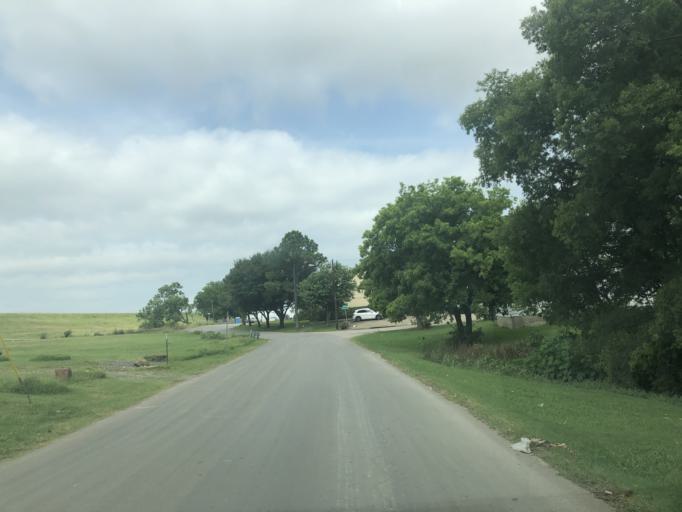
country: US
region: Texas
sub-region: Dallas County
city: Cockrell Hill
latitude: 32.8033
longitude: -96.8786
